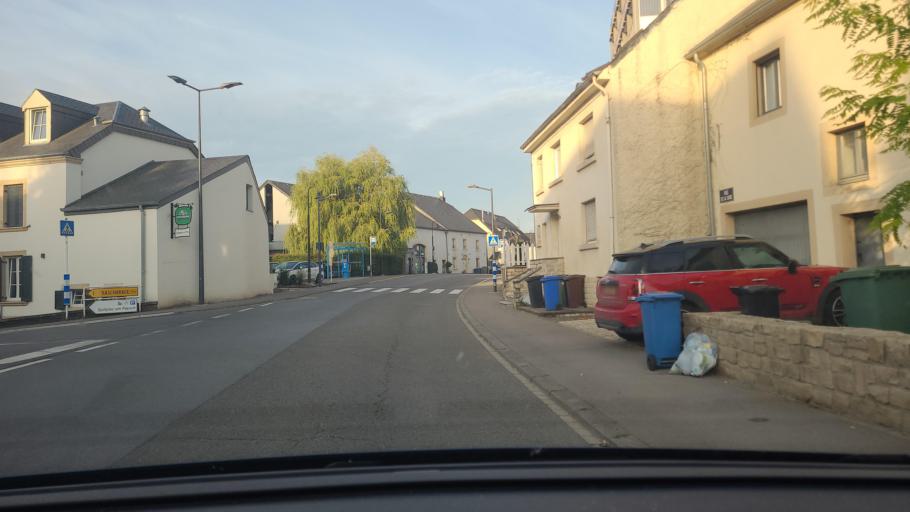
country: LU
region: Luxembourg
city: Hautcharage
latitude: 49.5773
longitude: 5.9102
